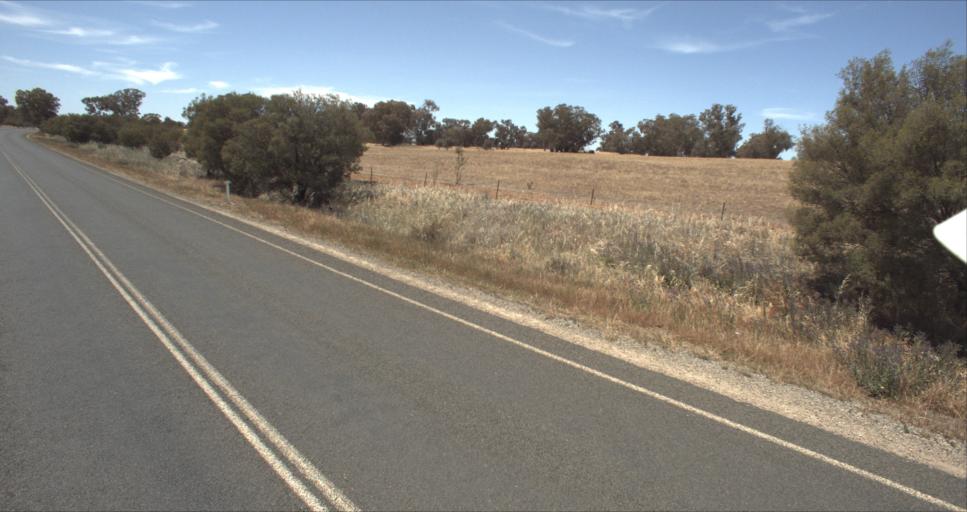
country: AU
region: New South Wales
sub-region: Leeton
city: Leeton
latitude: -34.6613
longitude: 146.4514
